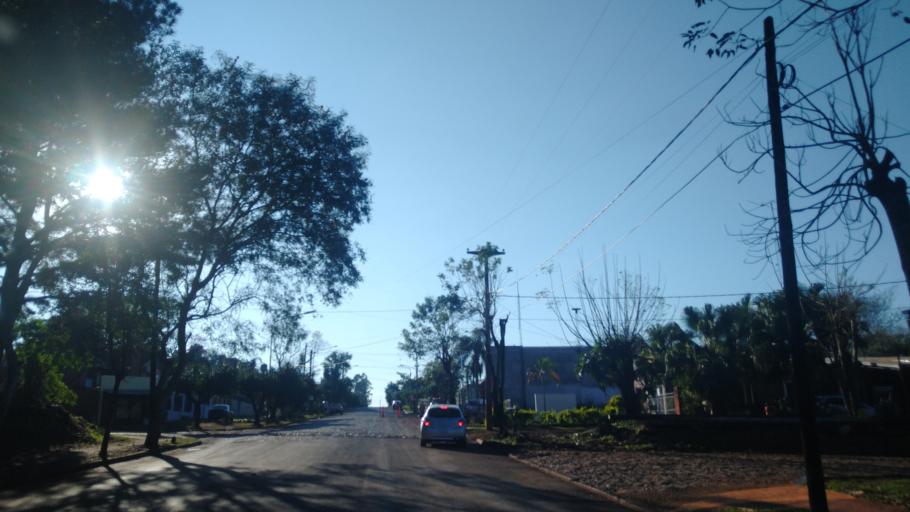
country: AR
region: Misiones
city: Puerto Libertad
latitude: -25.9717
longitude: -54.5577
